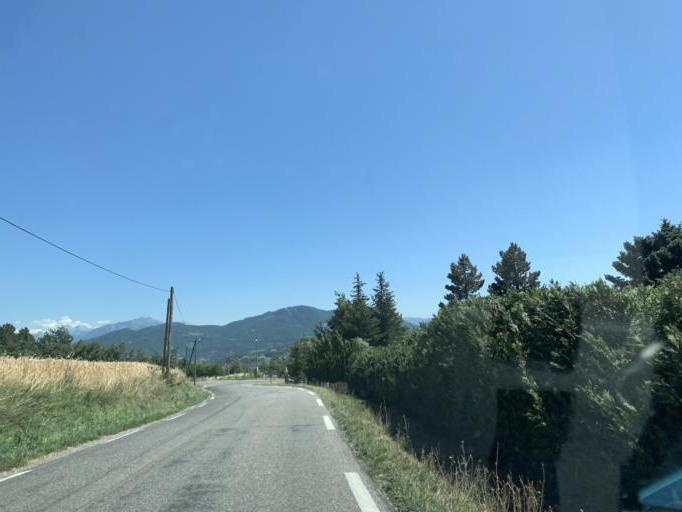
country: FR
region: Provence-Alpes-Cote d'Azur
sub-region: Departement des Hautes-Alpes
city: La Batie-Neuve
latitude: 44.5907
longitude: 6.1545
